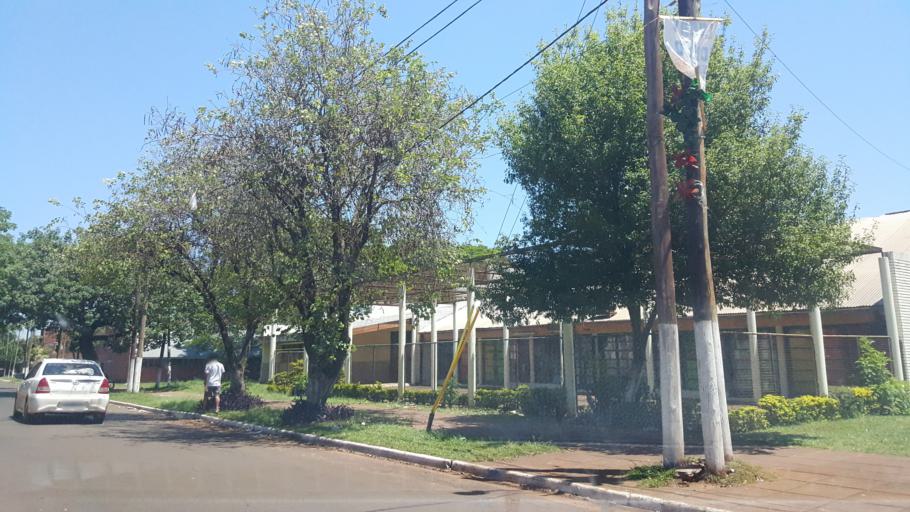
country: AR
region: Misiones
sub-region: Departamento de Capital
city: Posadas
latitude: -27.3749
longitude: -55.9252
